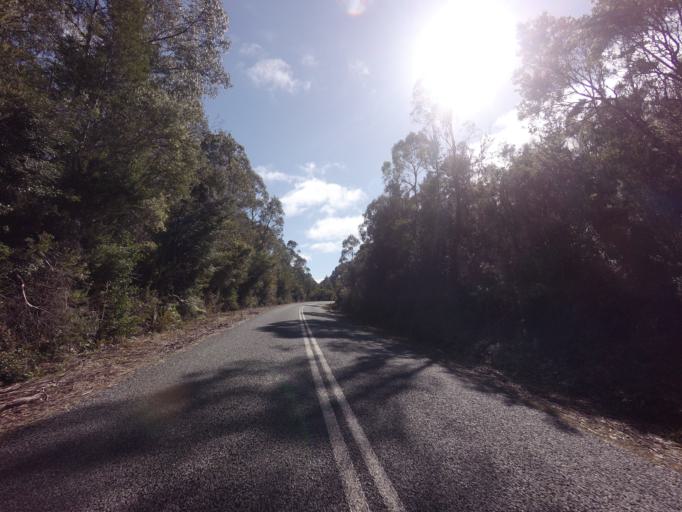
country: AU
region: Tasmania
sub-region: Huon Valley
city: Geeveston
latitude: -42.8085
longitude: 146.3921
